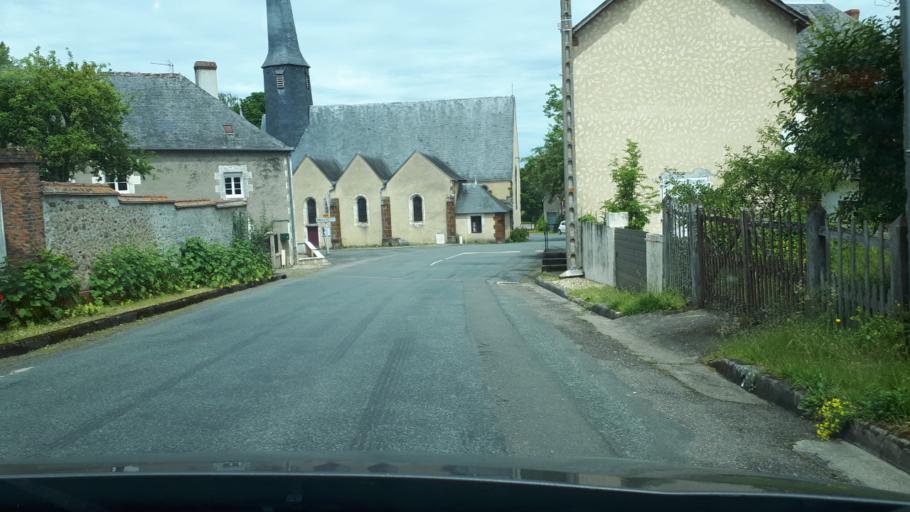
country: FR
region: Centre
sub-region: Departement du Cher
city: Blancafort
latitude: 47.4263
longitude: 2.6051
